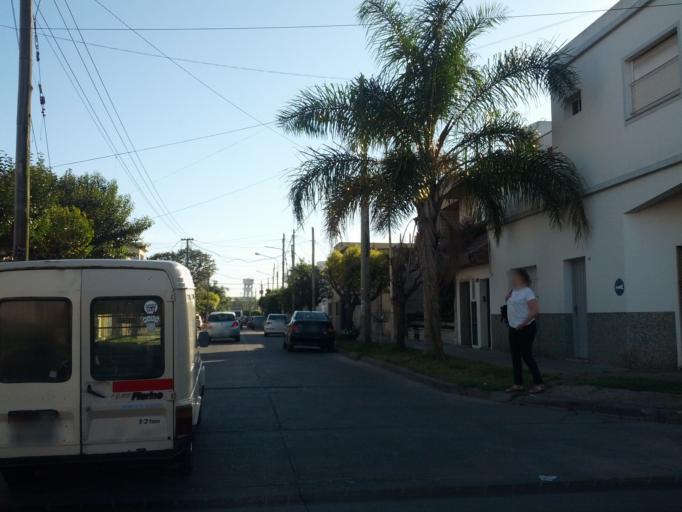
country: AR
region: Buenos Aires
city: San Justo
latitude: -34.6591
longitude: -58.5274
